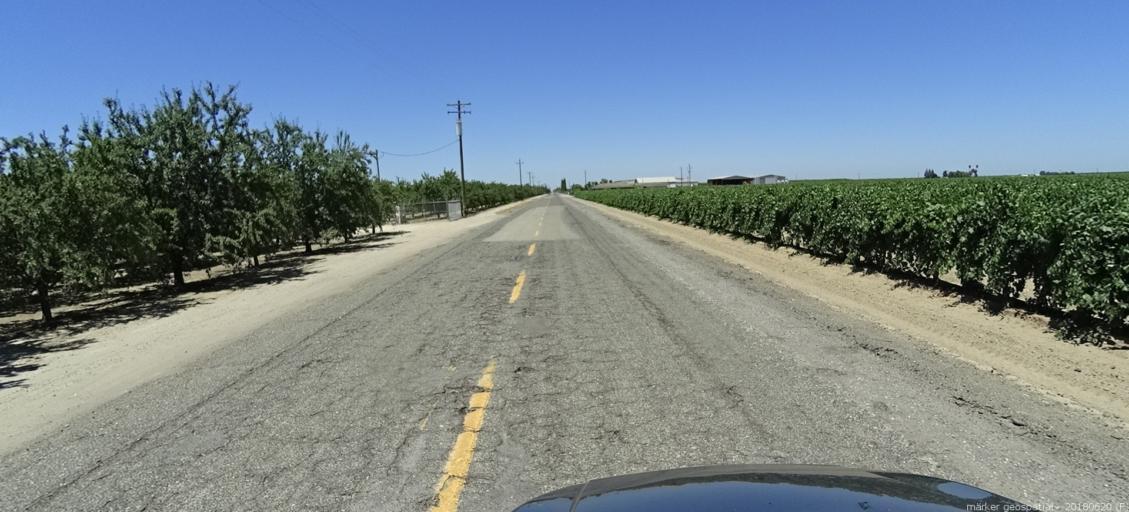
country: US
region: California
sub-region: Madera County
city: Parkwood
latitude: 36.8659
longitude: -120.0484
